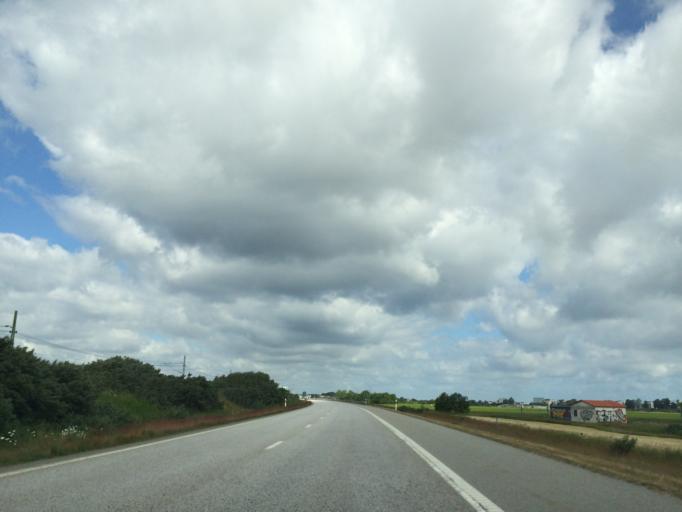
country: SE
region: Skane
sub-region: Malmo
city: Bunkeflostrand
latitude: 55.5592
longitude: 12.9399
